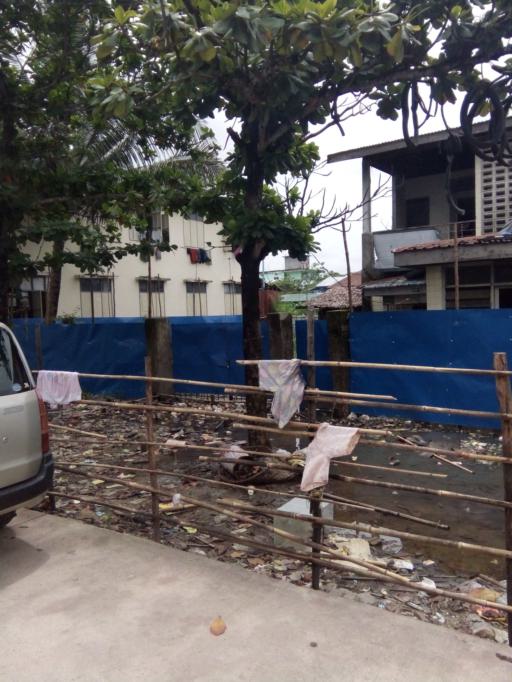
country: MM
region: Yangon
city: Yangon
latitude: 16.8670
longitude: 96.0602
